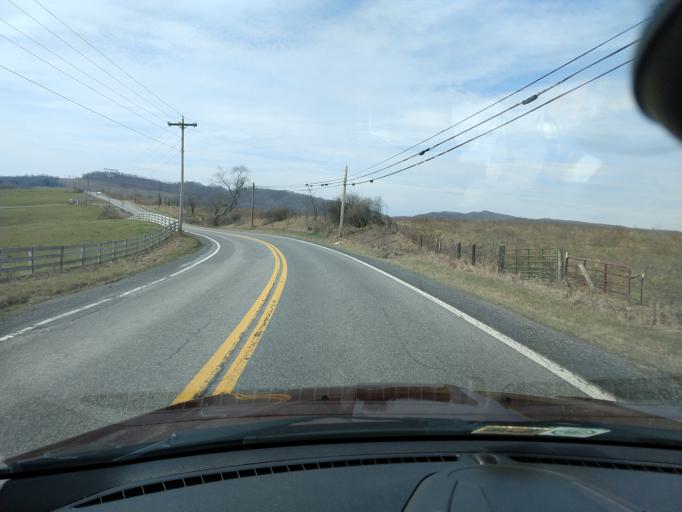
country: US
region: West Virginia
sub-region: Greenbrier County
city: Lewisburg
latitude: 37.9003
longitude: -80.4027
